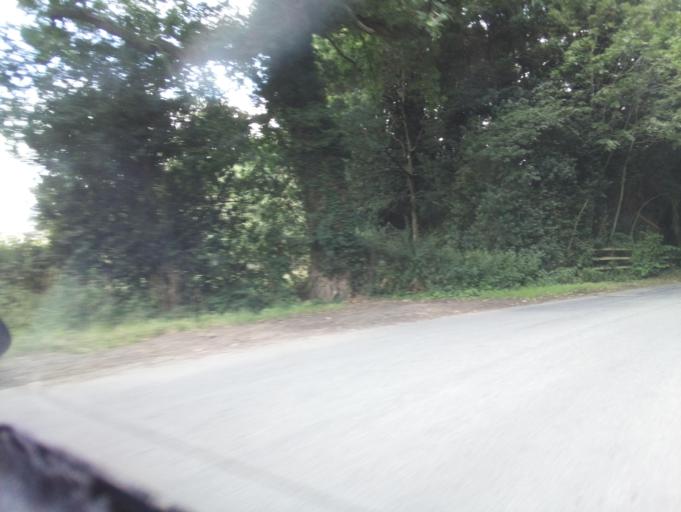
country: GB
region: England
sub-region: Wiltshire
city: Minety
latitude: 51.6141
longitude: -1.9862
